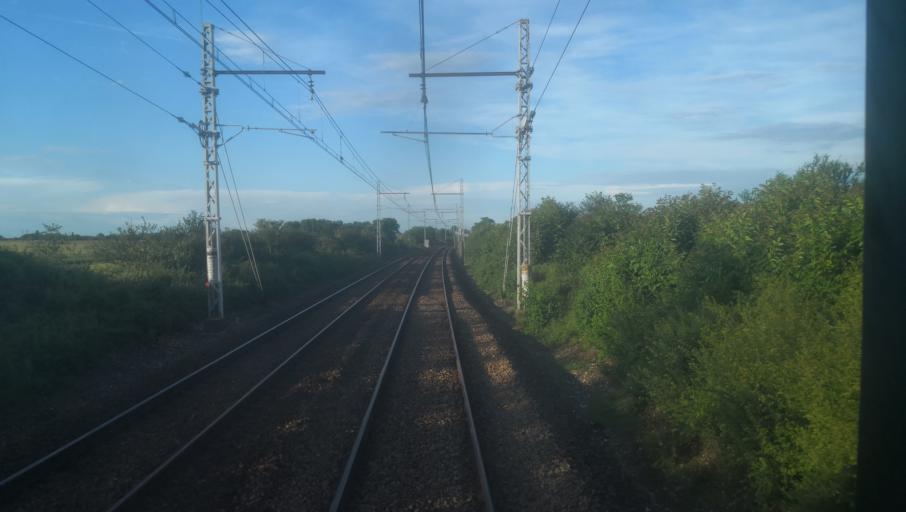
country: FR
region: Centre
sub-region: Departement de l'Indre
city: Saint-Maur
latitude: 46.7882
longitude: 1.6511
